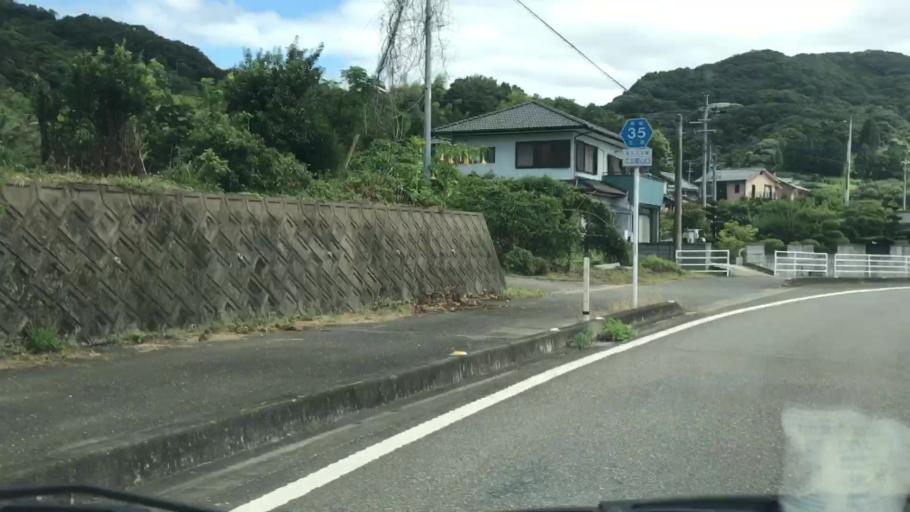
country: JP
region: Saga Prefecture
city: Takeocho-takeo
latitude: 33.2329
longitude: 130.1510
